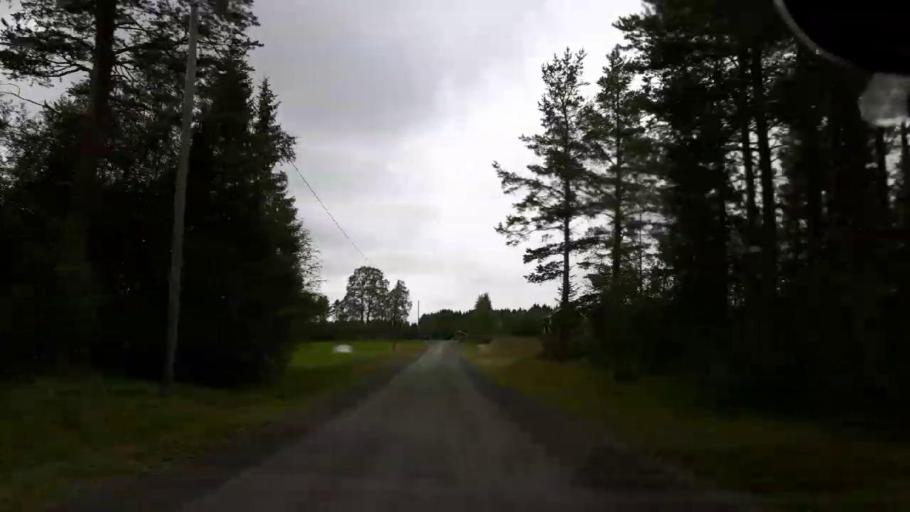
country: SE
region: Jaemtland
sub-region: OEstersunds Kommun
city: Ostersund
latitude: 63.0444
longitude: 14.5752
